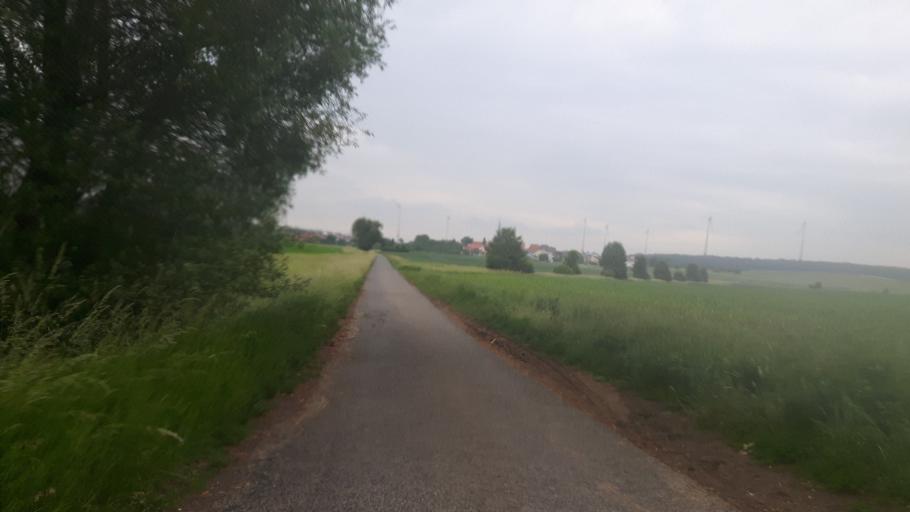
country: DE
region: Bavaria
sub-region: Regierungsbezirk Unterfranken
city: Oberpleichfeld
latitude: 49.8939
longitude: 10.1125
